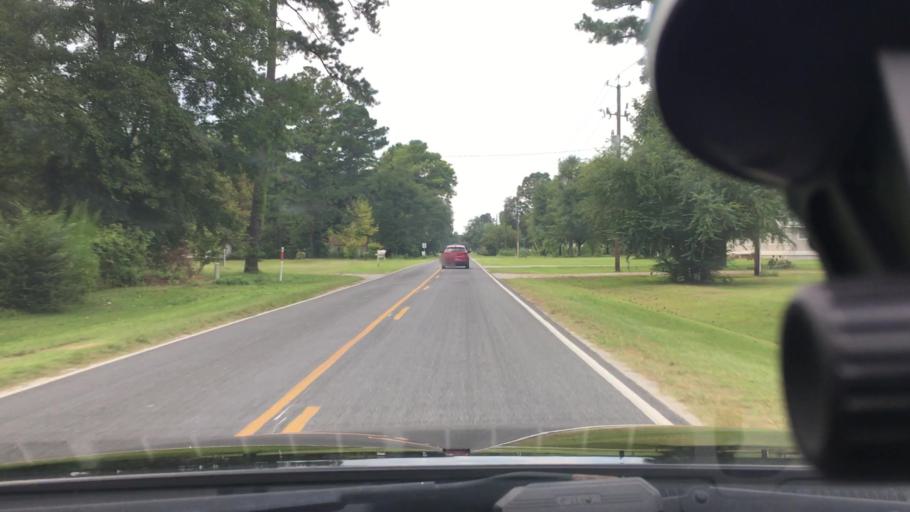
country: US
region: North Carolina
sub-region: Craven County
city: New Bern
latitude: 35.1741
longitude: -77.0519
